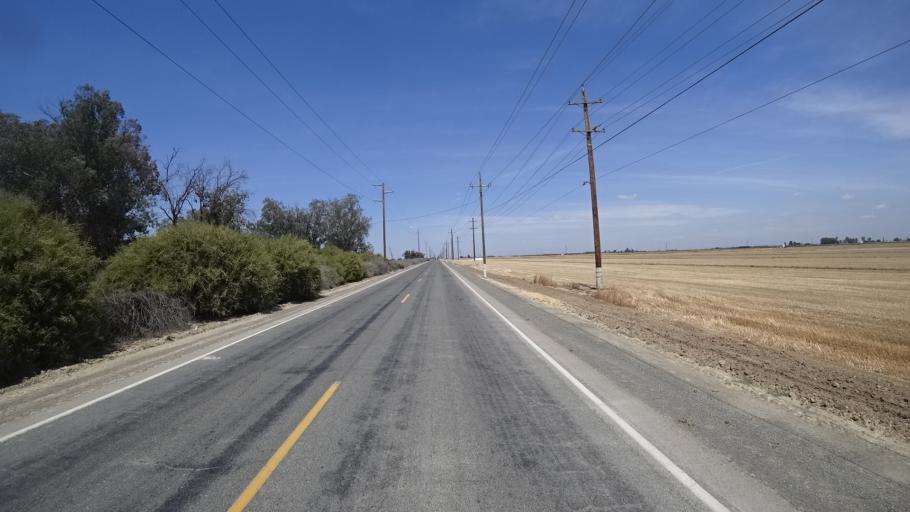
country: US
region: California
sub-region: Kings County
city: Home Garden
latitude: 36.2154
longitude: -119.6549
